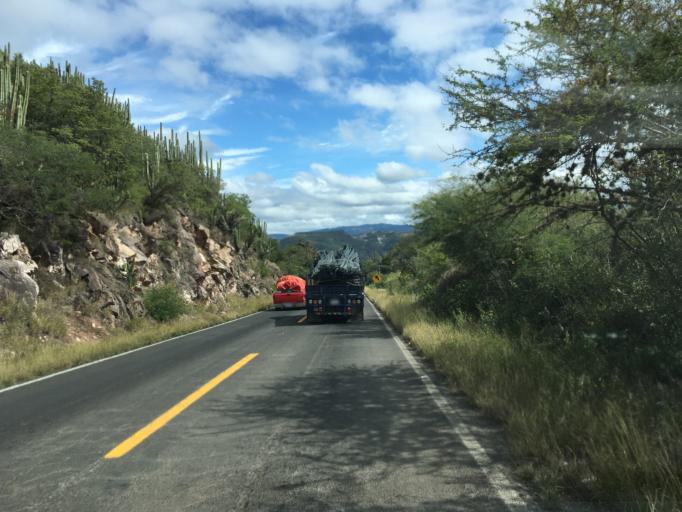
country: MX
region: Hidalgo
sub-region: San Agustin Metzquititlan
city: Mezquititlan
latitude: 20.4415
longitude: -98.6827
